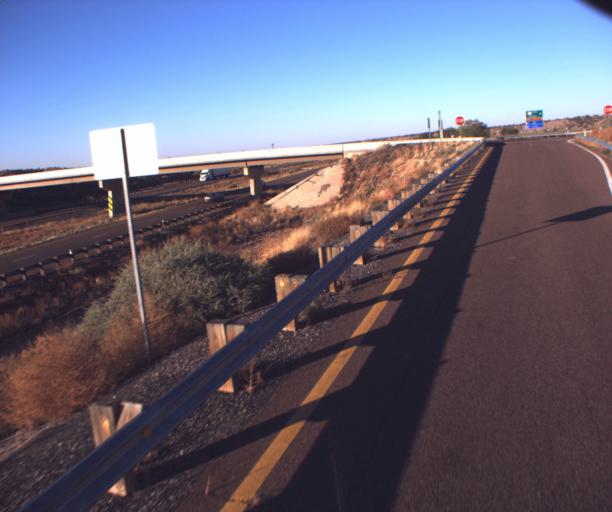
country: US
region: Arizona
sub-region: Apache County
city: Houck
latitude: 35.1910
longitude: -109.4352
